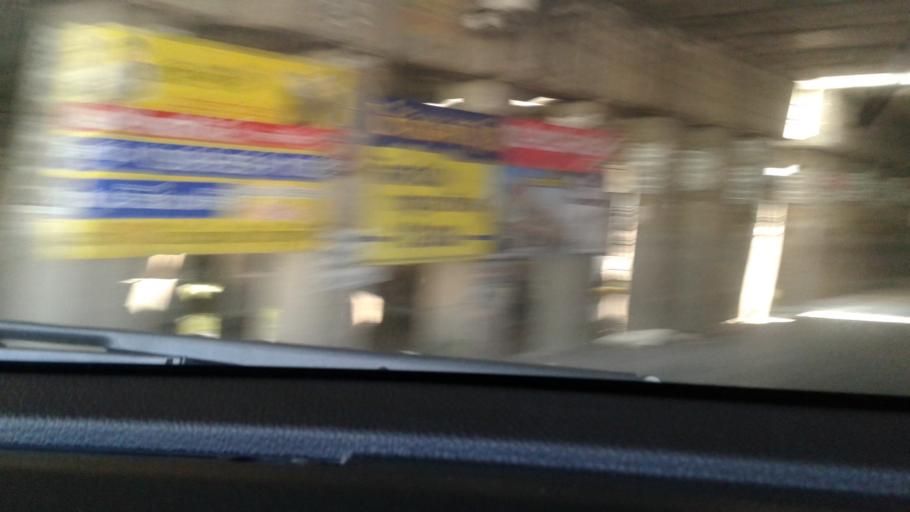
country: TH
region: Nonthaburi
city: Bang Bua Thong
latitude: 13.9522
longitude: 100.4240
